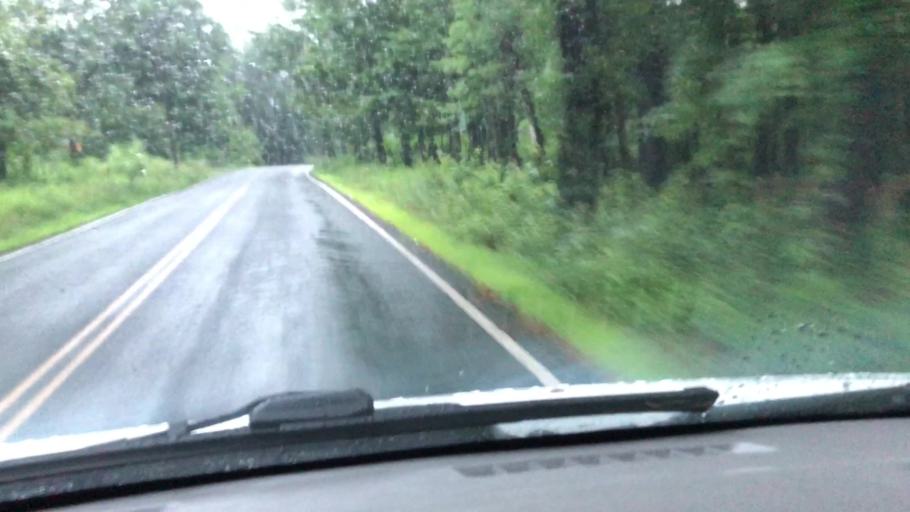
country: US
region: Massachusetts
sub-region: Hampshire County
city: Westhampton
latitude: 42.2803
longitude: -72.7548
